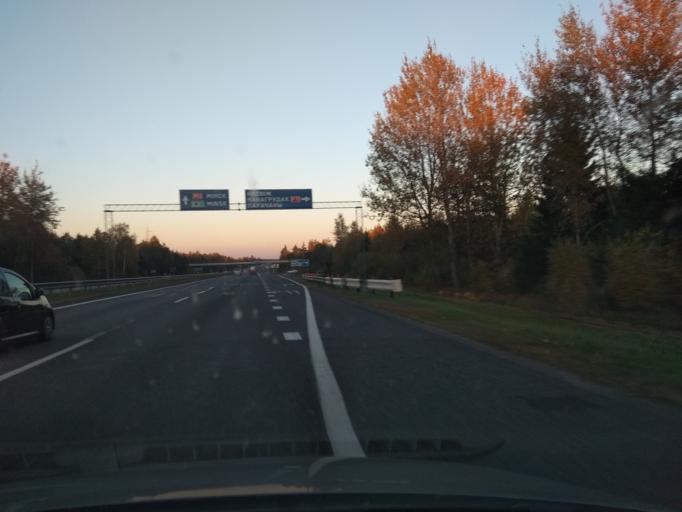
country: BY
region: Minsk
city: Haradzyeya
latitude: 53.3790
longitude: 26.5058
